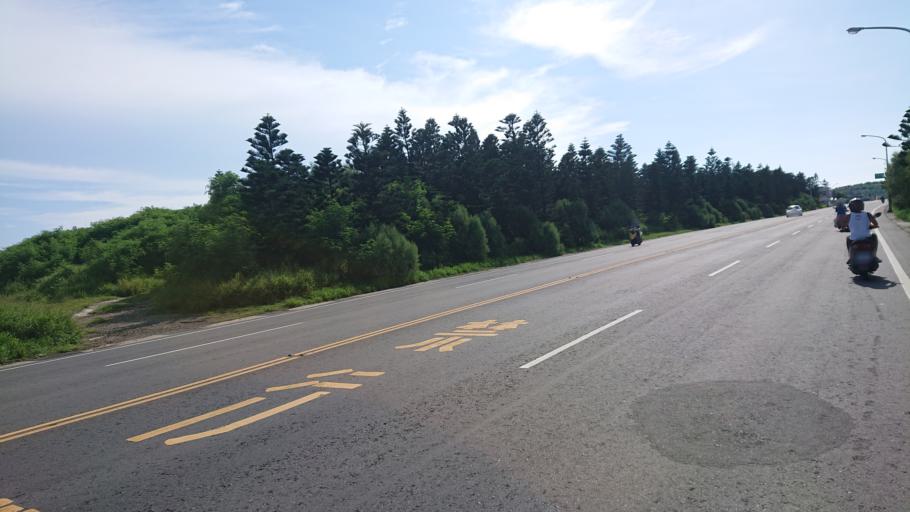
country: TW
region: Taiwan
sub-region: Penghu
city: Ma-kung
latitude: 23.5267
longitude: 119.5930
